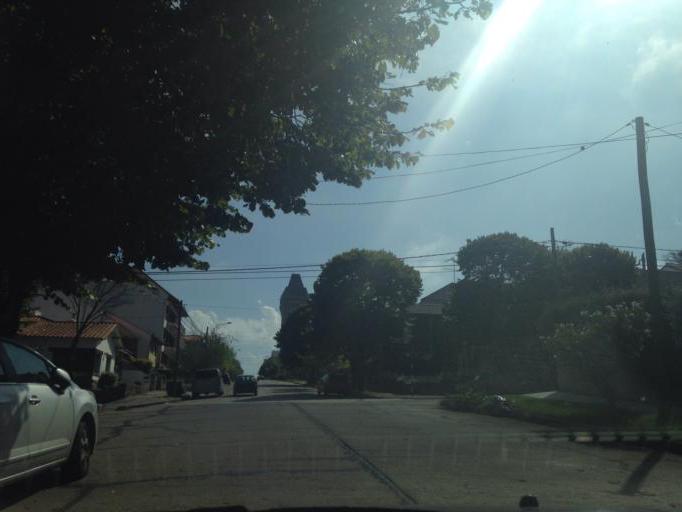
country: AR
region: Buenos Aires
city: Mar del Plata
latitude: -38.0151
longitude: -57.5370
